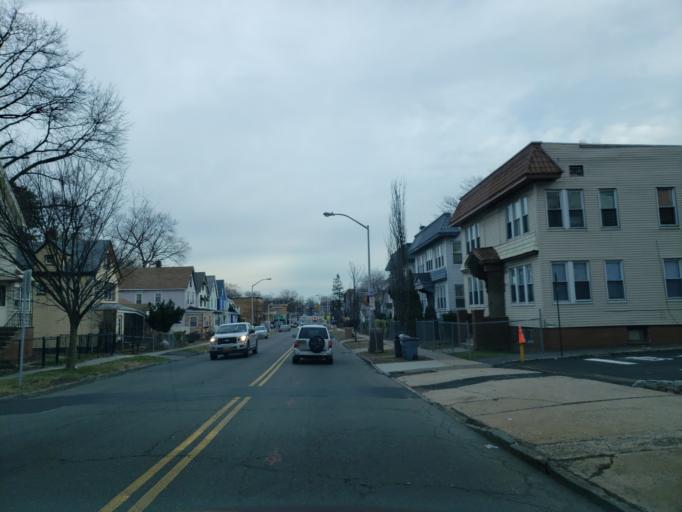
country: US
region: New Jersey
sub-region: Essex County
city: East Orange
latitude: 40.7739
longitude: -74.2082
